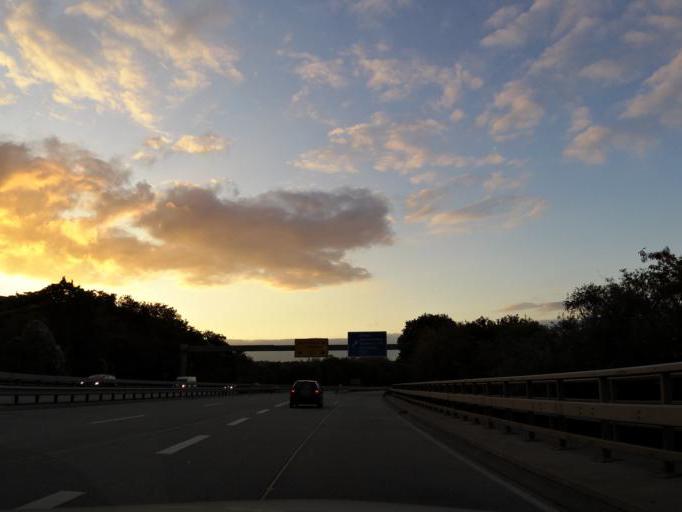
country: DE
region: Hesse
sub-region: Regierungsbezirk Darmstadt
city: Ginsheim-Gustavsburg
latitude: 49.9684
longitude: 8.3145
